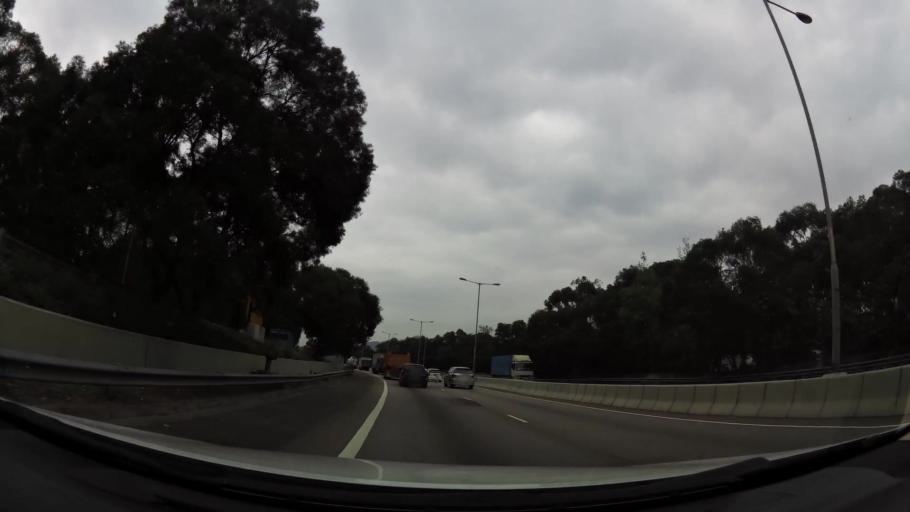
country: HK
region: Yuen Long
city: Yuen Long Kau Hui
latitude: 22.4384
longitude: 114.0379
